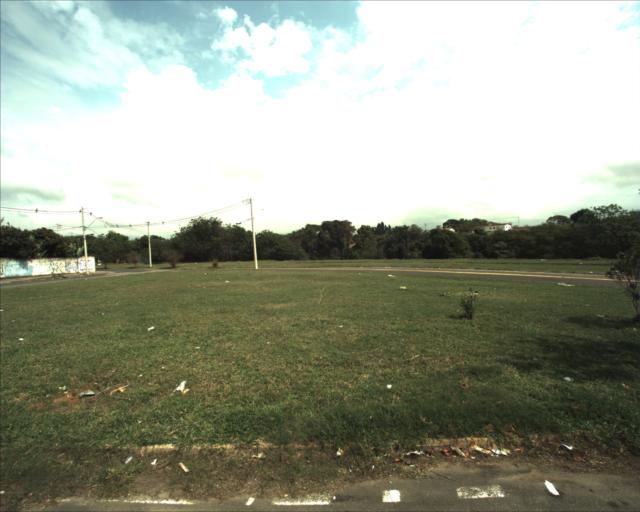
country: BR
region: Sao Paulo
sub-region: Sorocaba
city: Sorocaba
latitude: -23.4291
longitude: -47.5139
